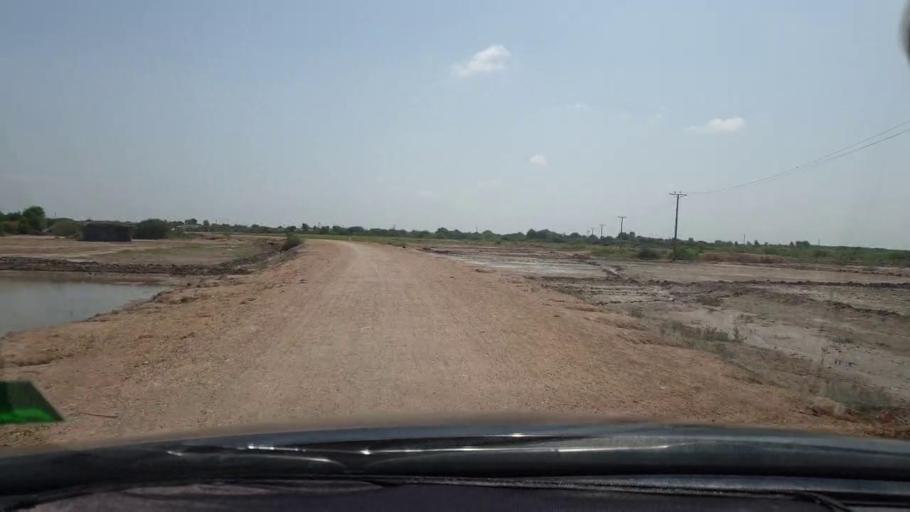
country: PK
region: Sindh
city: Tando Bago
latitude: 24.8902
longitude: 69.0993
